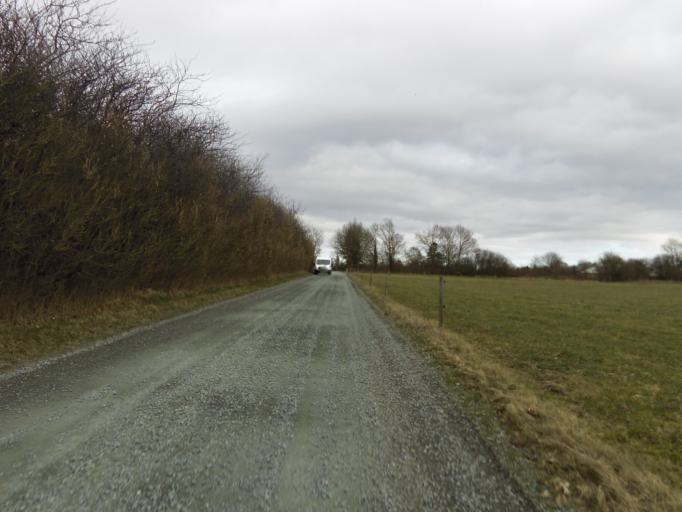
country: DK
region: South Denmark
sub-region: Tonder Kommune
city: Toftlund
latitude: 55.2115
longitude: 9.1719
